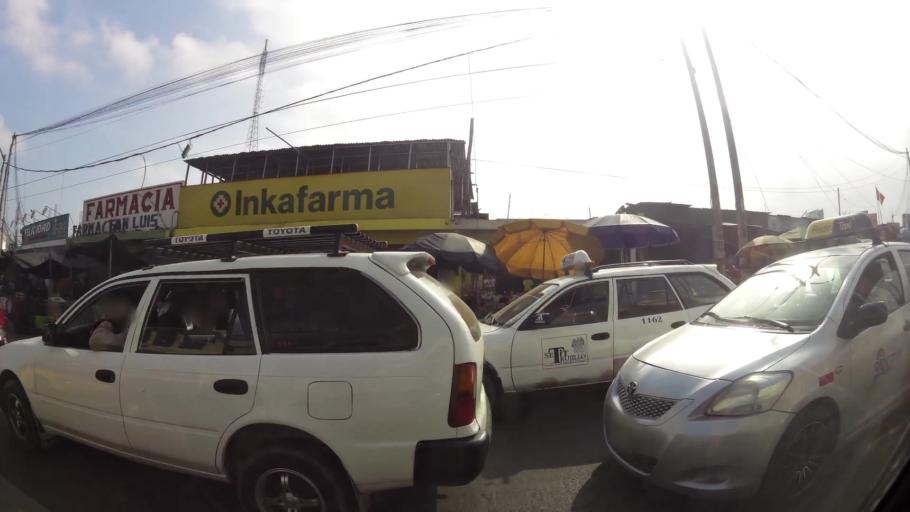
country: PE
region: La Libertad
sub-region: Provincia de Trujillo
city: Trujillo
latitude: -8.1104
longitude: -79.0200
